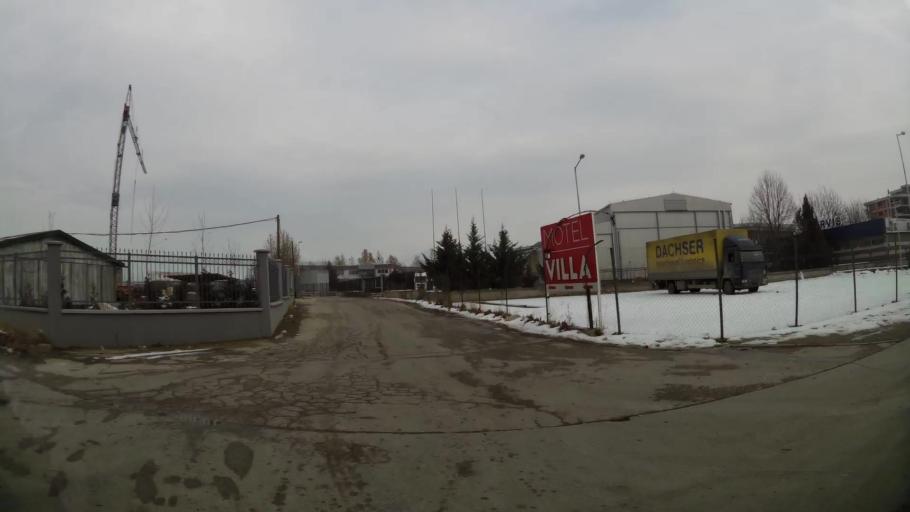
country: MK
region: Suto Orizari
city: Suto Orizare
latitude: 42.0444
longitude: 21.3891
